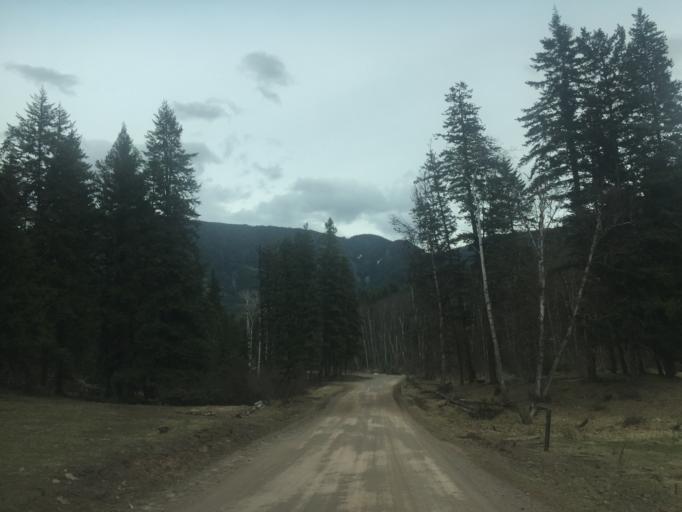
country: CA
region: British Columbia
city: Chase
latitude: 51.3745
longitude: -120.1487
